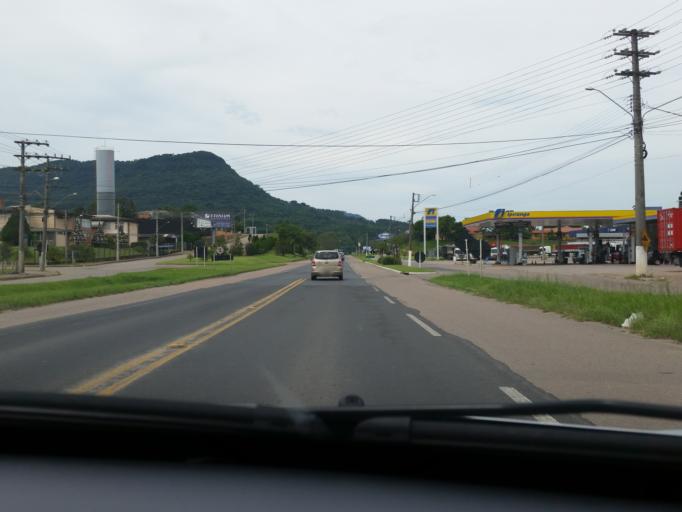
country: BR
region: Santa Catarina
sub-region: Rio Do Sul
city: Rio do Sul
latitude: -27.1974
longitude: -49.6281
